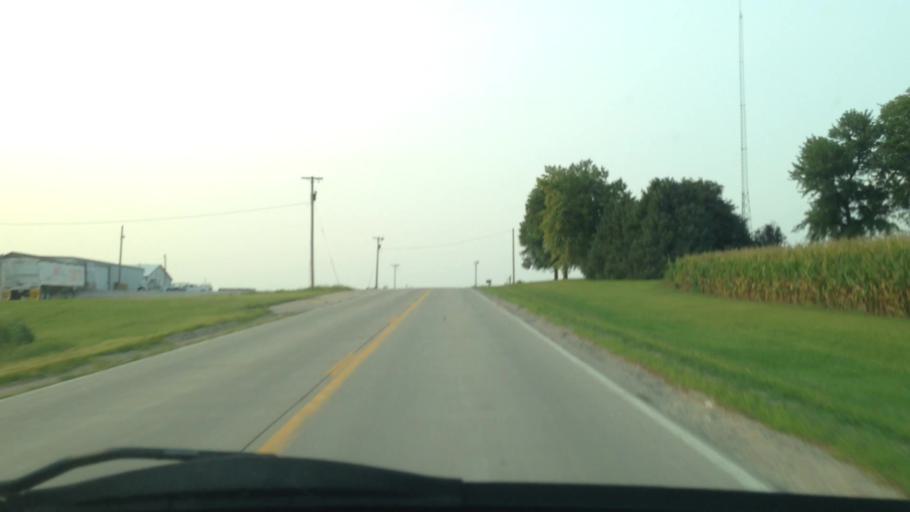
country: US
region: Iowa
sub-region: Benton County
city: Atkins
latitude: 41.9683
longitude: -91.8727
